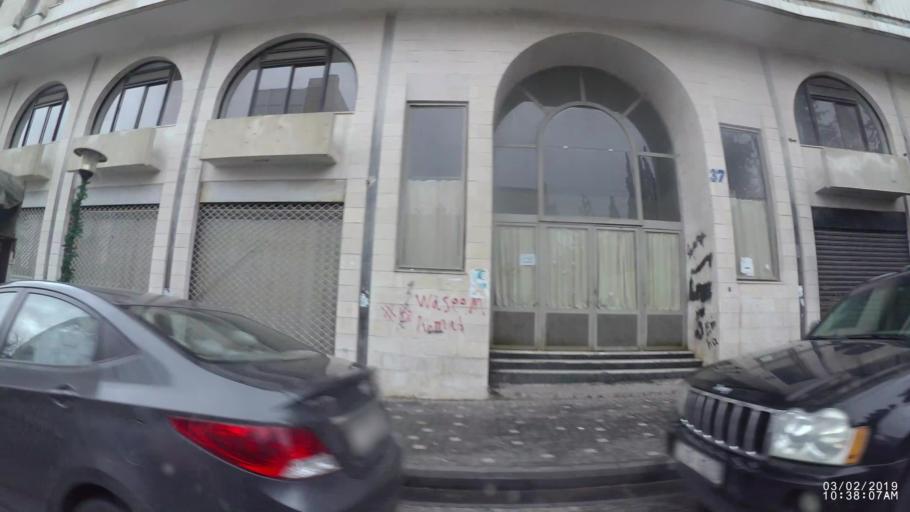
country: JO
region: Amman
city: Amman
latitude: 31.9495
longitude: 35.9261
